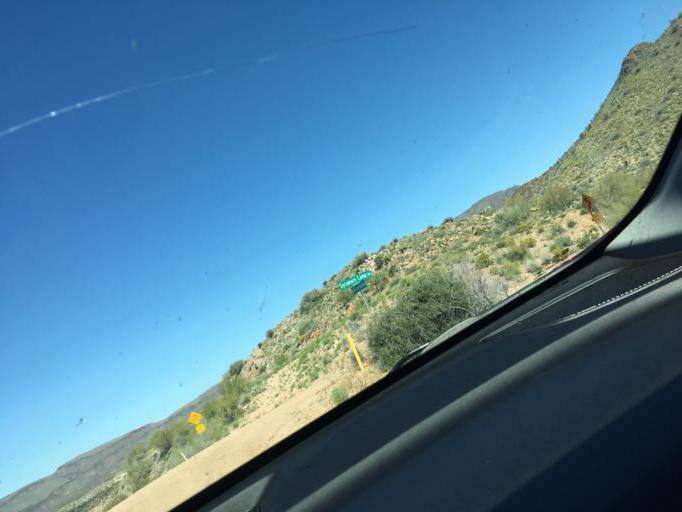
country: US
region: Arizona
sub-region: Yavapai County
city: Bagdad
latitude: 34.6100
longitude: -113.4029
